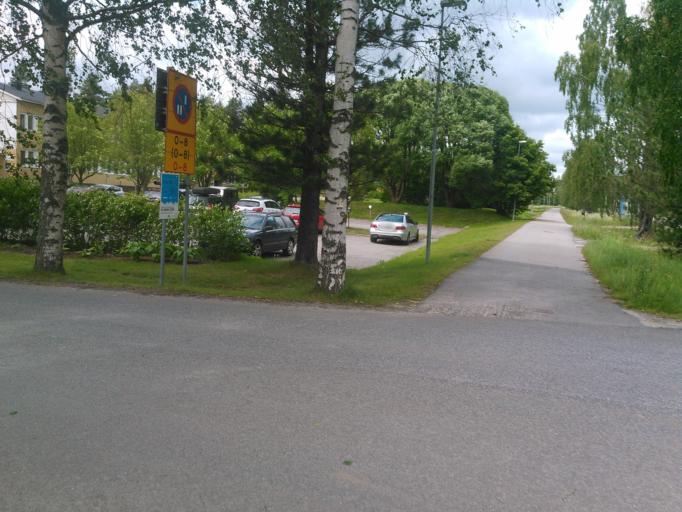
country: SE
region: Vaesterbotten
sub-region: Umea Kommun
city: Roback
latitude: 63.8645
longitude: 20.1988
